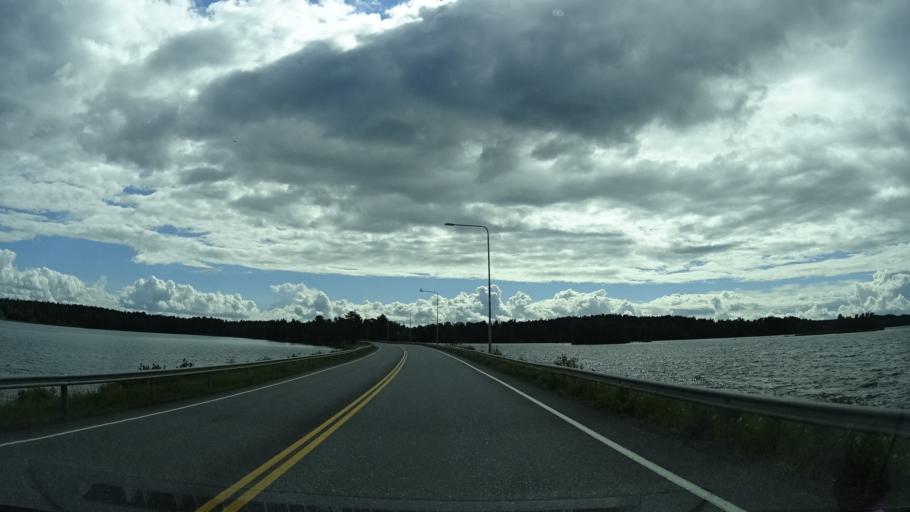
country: FI
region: Pirkanmaa
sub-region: Etelae-Pirkanmaa
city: Valkeakoski
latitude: 61.1795
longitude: 24.0370
